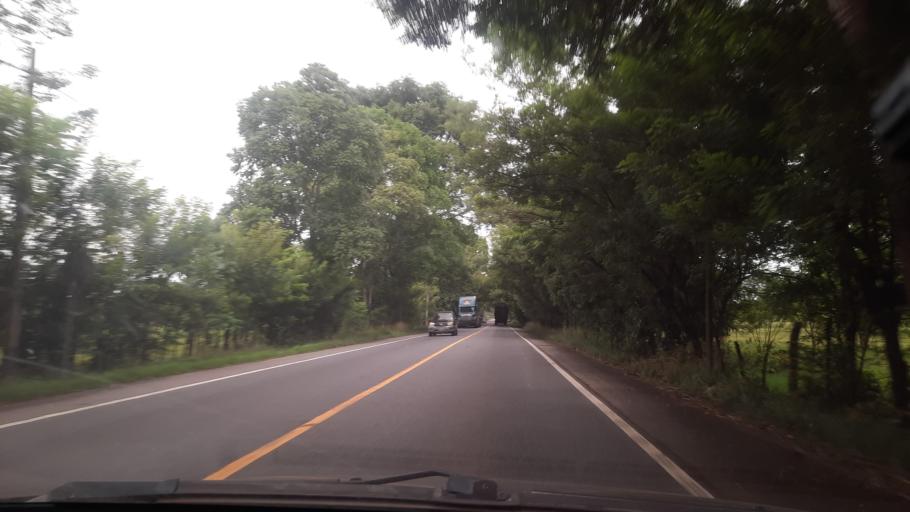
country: GT
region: Izabal
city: Morales
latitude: 15.4598
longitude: -88.9321
